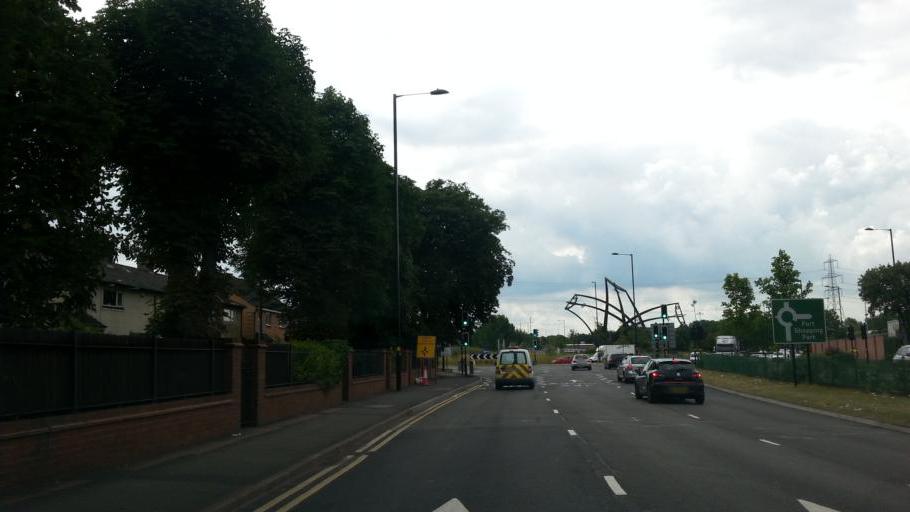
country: GB
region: England
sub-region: City and Borough of Birmingham
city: Sutton Coldfield
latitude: 52.5151
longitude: -1.7982
